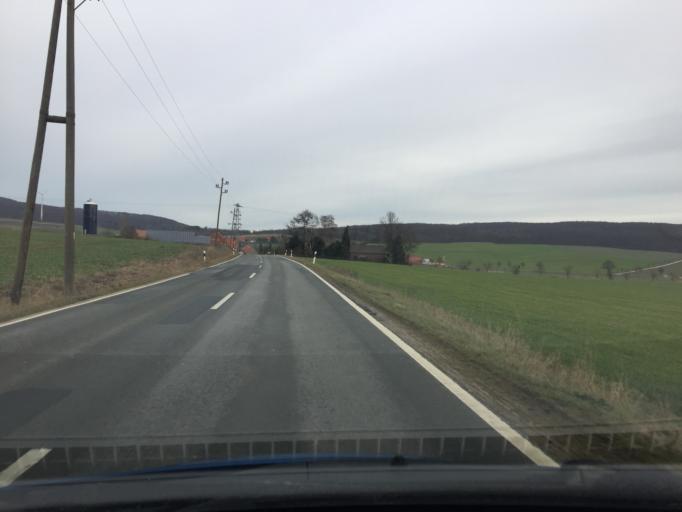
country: DE
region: Lower Saxony
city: Weenzen
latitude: 52.0147
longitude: 9.6666
